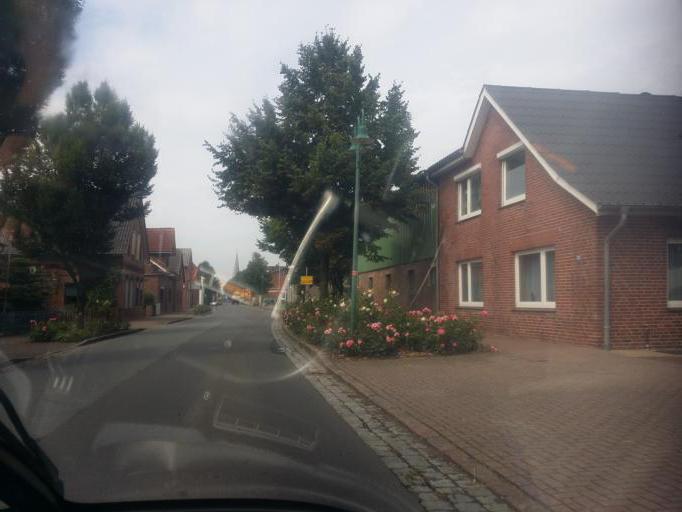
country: DE
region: Schleswig-Holstein
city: Eddelak
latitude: 53.9414
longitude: 9.1422
